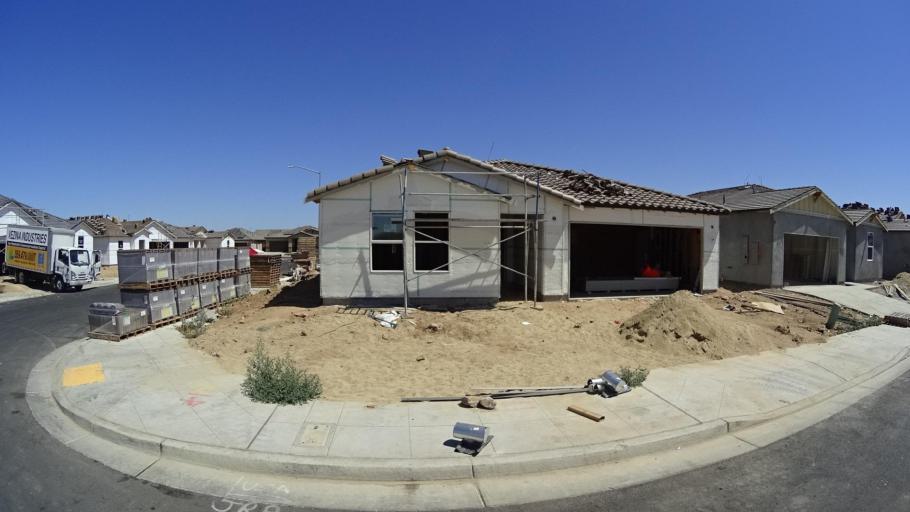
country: US
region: California
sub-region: Fresno County
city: Sunnyside
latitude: 36.7227
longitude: -119.6671
